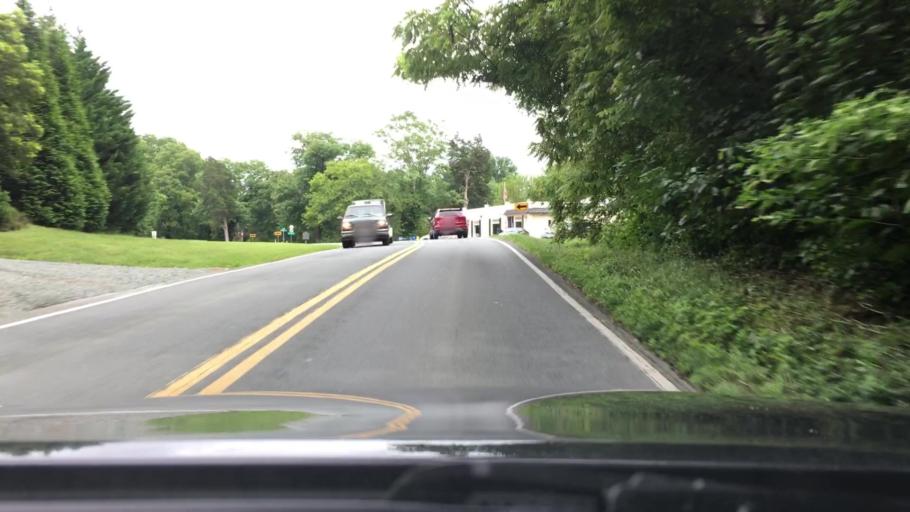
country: US
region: Virginia
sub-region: Fluvanna County
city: Lake Monticello
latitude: 38.0235
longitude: -78.3593
